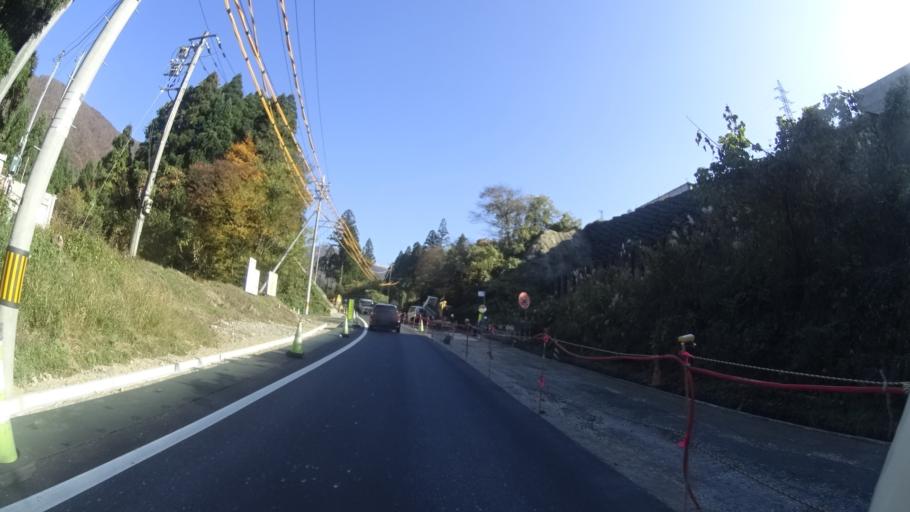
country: JP
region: Fukui
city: Ono
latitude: 35.9652
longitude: 136.5995
